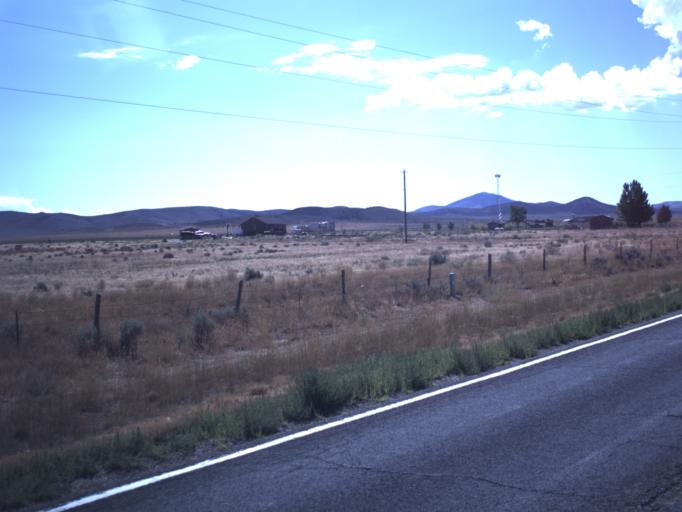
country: US
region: Utah
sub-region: Tooele County
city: Tooele
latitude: 40.0955
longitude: -112.4309
